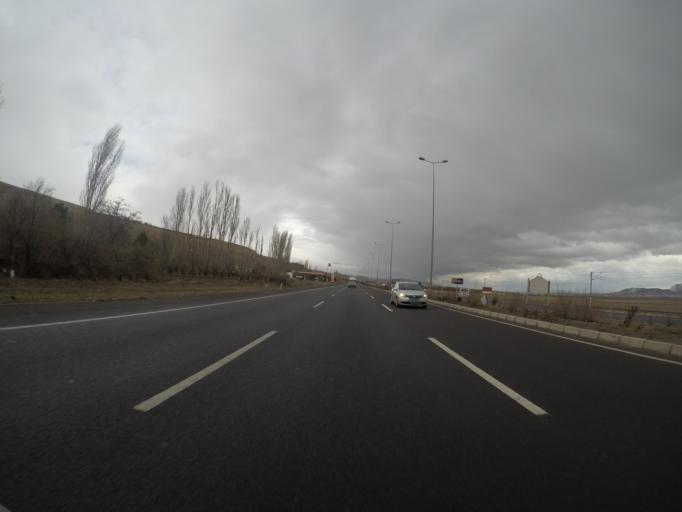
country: TR
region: Kayseri
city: Incesu
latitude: 38.7279
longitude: 35.2803
